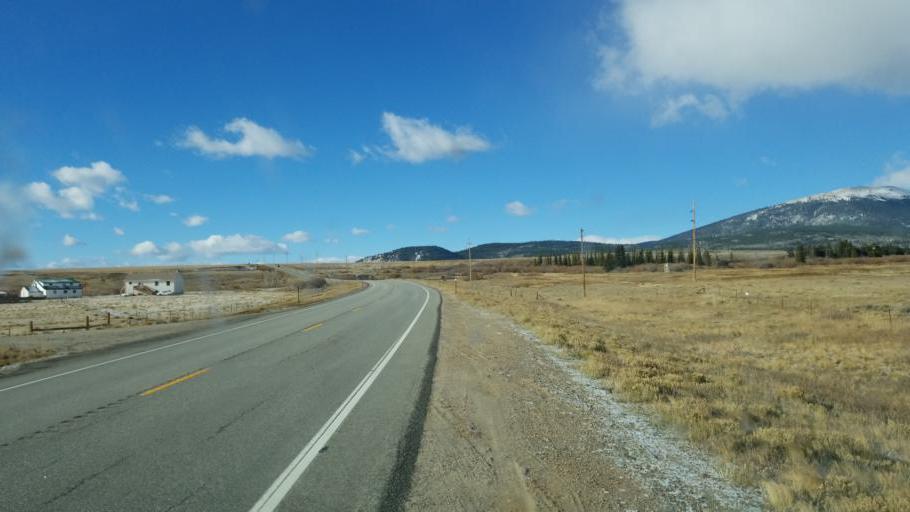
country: US
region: Colorado
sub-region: Park County
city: Fairplay
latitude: 39.3346
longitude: -105.8646
